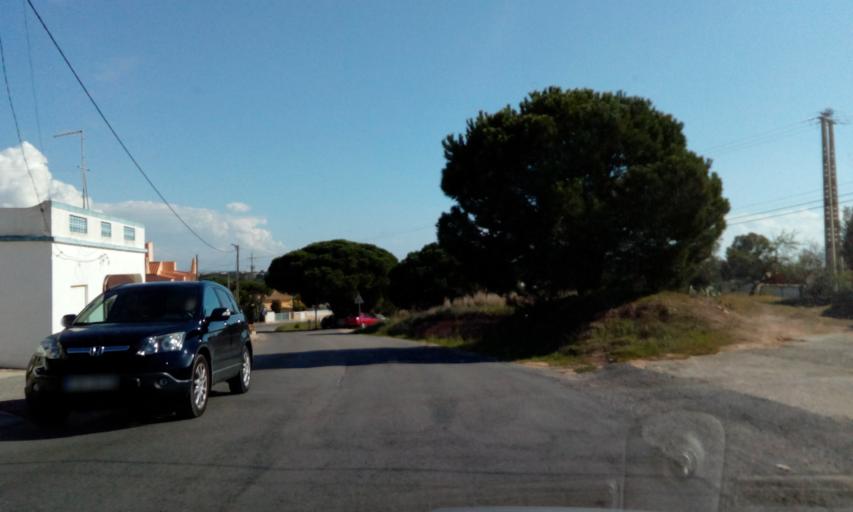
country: PT
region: Faro
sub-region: Albufeira
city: Ferreiras
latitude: 37.1166
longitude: -8.2141
